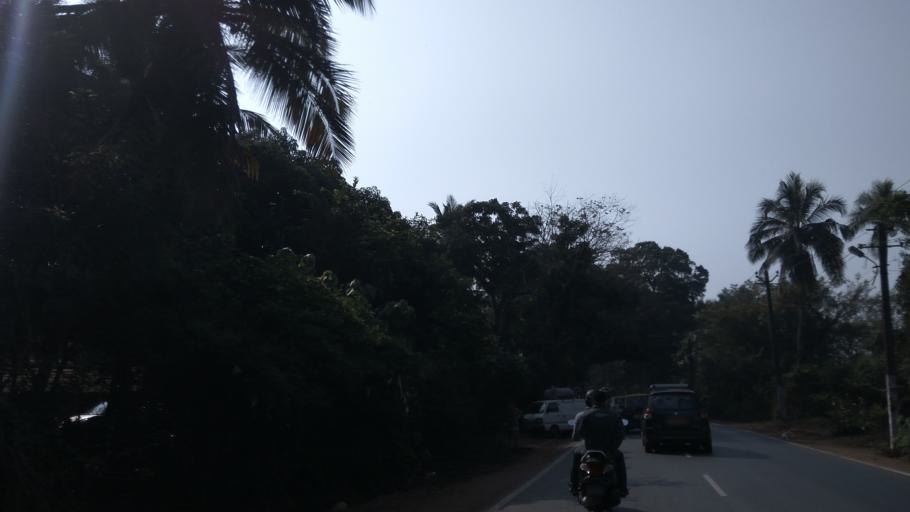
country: IN
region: Goa
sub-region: North Goa
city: Jua
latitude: 15.4844
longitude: 73.9588
